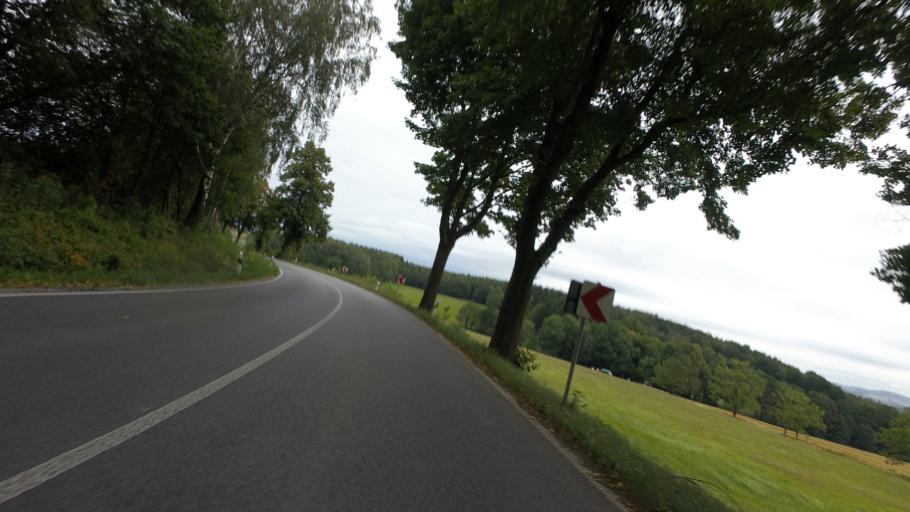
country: DE
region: Saxony
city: Berthelsdorf
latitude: 51.0823
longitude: 14.2022
